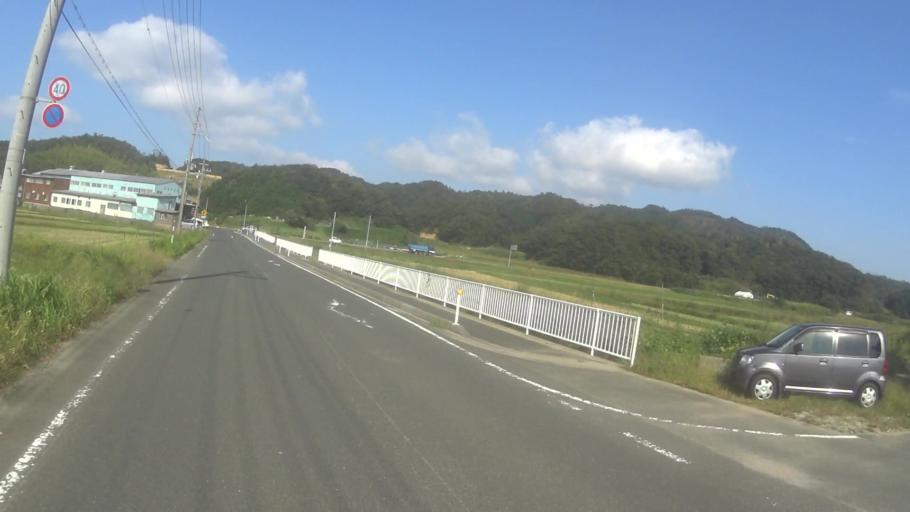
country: JP
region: Kyoto
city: Miyazu
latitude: 35.6875
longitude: 135.0516
